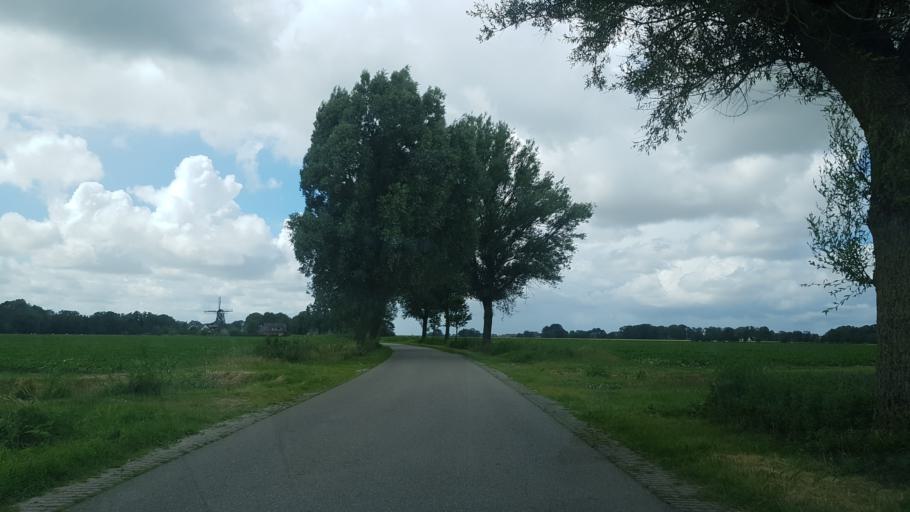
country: NL
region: Groningen
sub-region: Gemeente Winsum
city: Winsum
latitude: 53.3974
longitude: 6.4676
